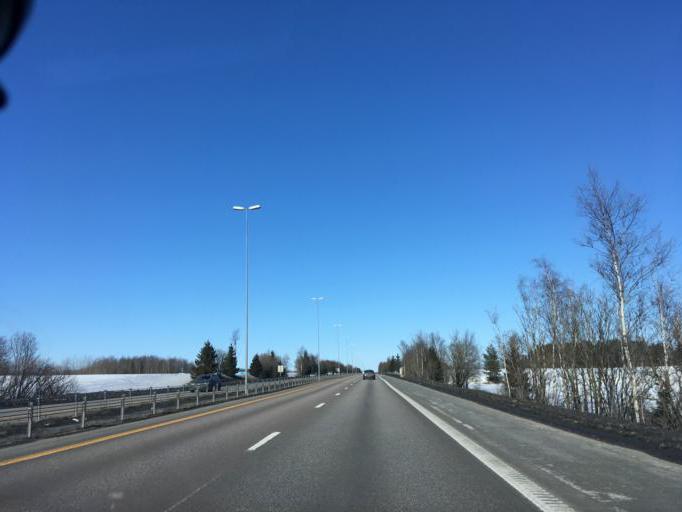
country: NO
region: Akershus
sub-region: Ullensaker
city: Klofta
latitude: 60.0894
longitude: 11.1469
